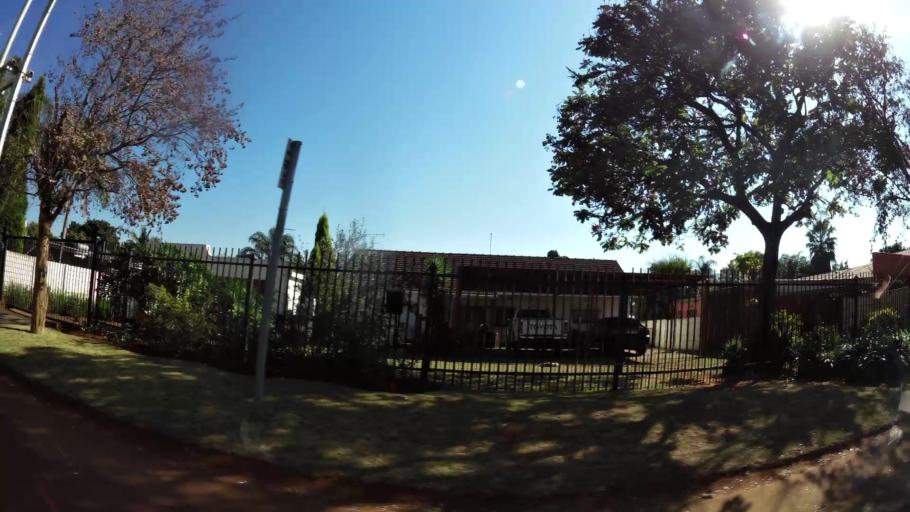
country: ZA
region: Gauteng
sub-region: City of Tshwane Metropolitan Municipality
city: Pretoria
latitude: -25.6754
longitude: 28.2104
